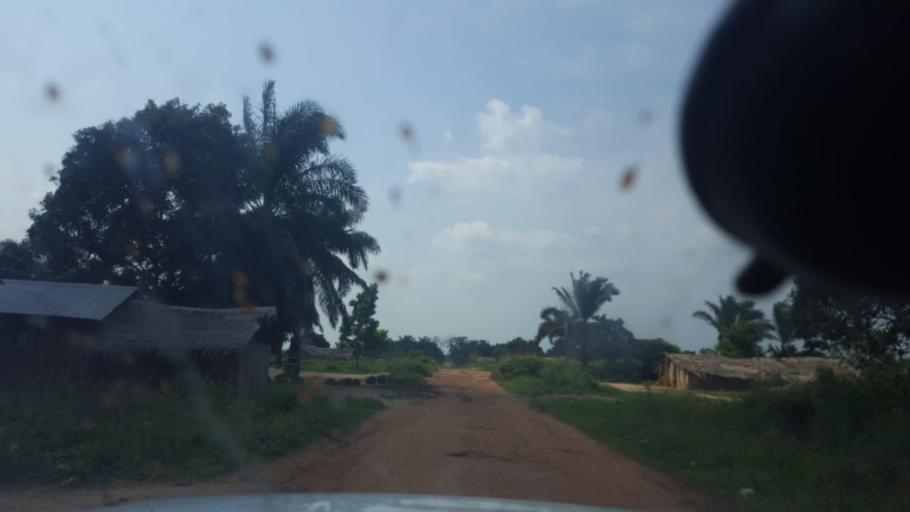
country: CD
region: Bandundu
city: Bandundu
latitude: -3.7540
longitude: 17.0398
